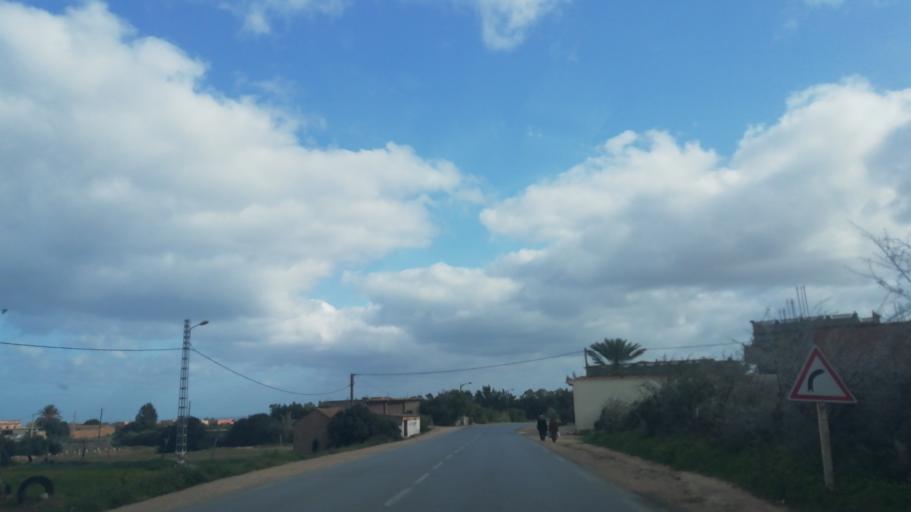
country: DZ
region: Relizane
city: Mazouna
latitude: 36.2783
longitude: 0.6373
